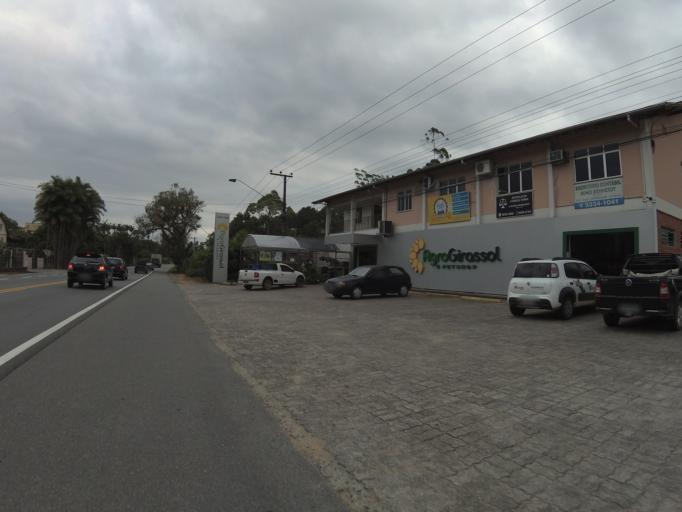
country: BR
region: Santa Catarina
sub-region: Blumenau
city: Blumenau
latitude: -26.8686
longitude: -49.1424
